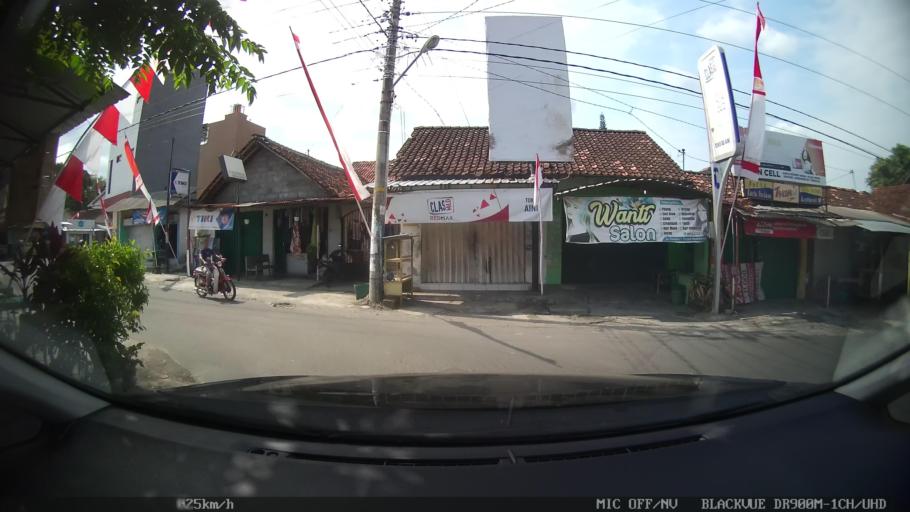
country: ID
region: Daerah Istimewa Yogyakarta
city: Depok
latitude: -7.7562
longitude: 110.4230
